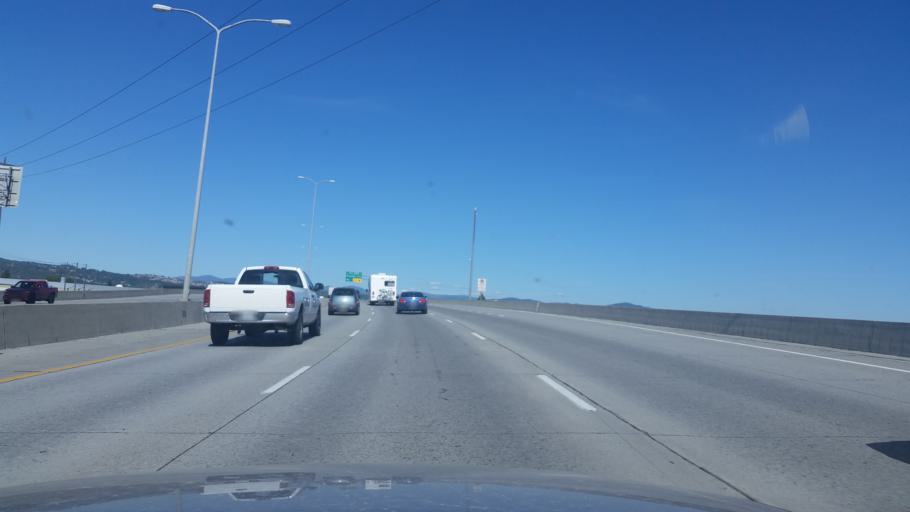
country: US
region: Washington
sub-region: Spokane County
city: Dishman
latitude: 47.6557
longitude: -117.3232
